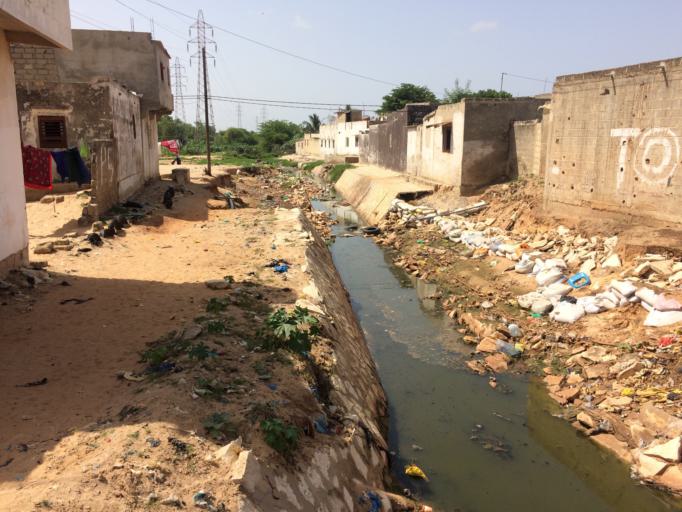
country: SN
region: Dakar
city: Pikine
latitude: 14.7480
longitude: -17.3116
